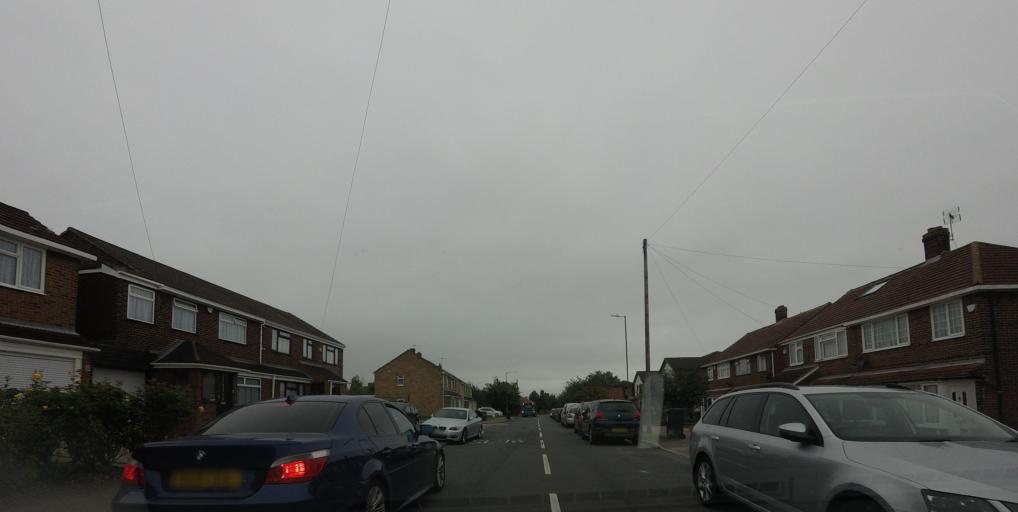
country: GB
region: England
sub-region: Kent
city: Stone
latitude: 51.4356
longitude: 0.2481
